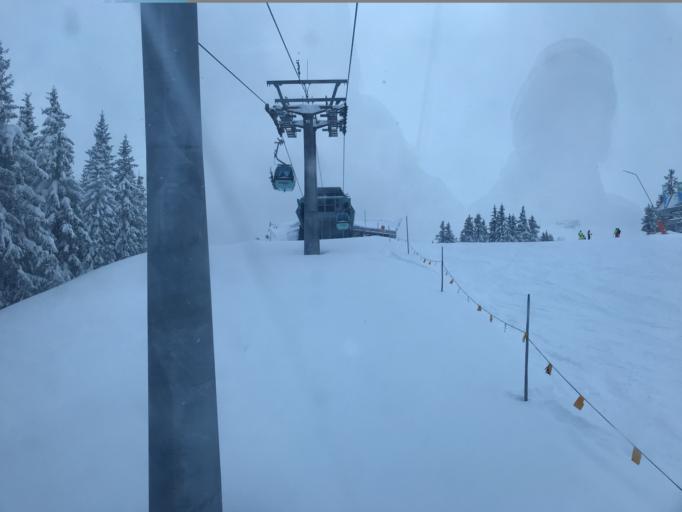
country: AT
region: Salzburg
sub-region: Politischer Bezirk Zell am See
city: Kaprun
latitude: 47.3149
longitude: 12.7513
